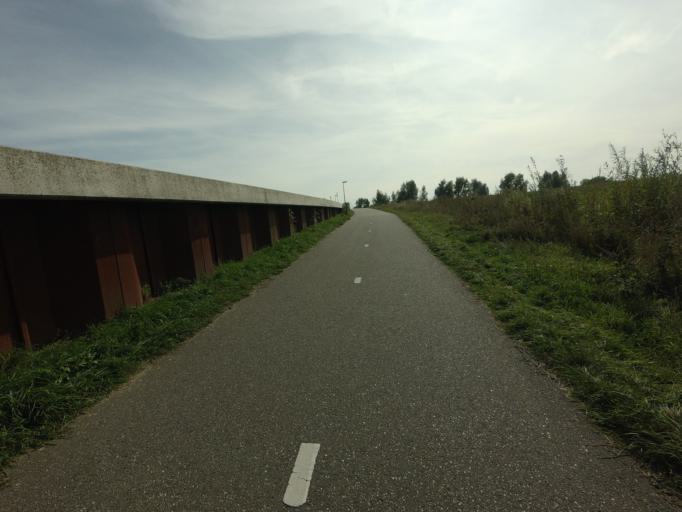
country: NL
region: Limburg
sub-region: Gemeente Roermond
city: Roermond
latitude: 51.1786
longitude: 5.9516
